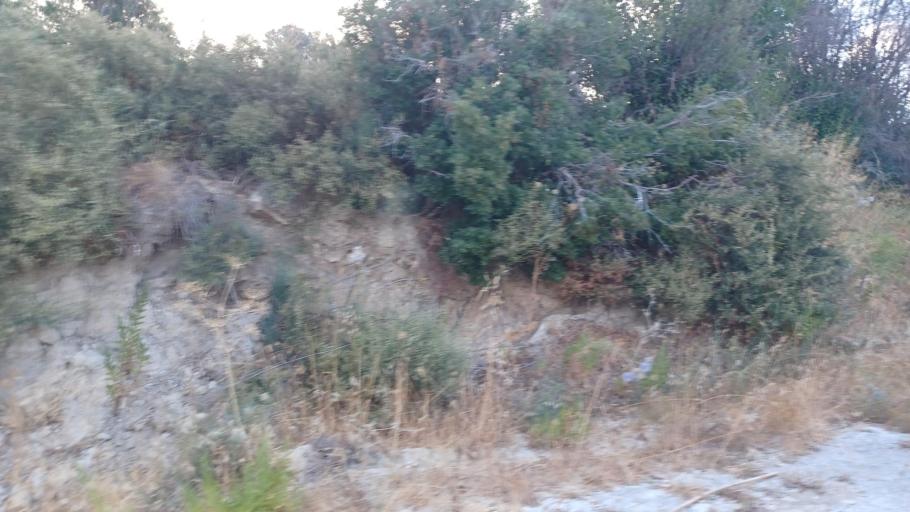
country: CY
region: Pafos
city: Mesogi
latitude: 34.8217
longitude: 32.5741
